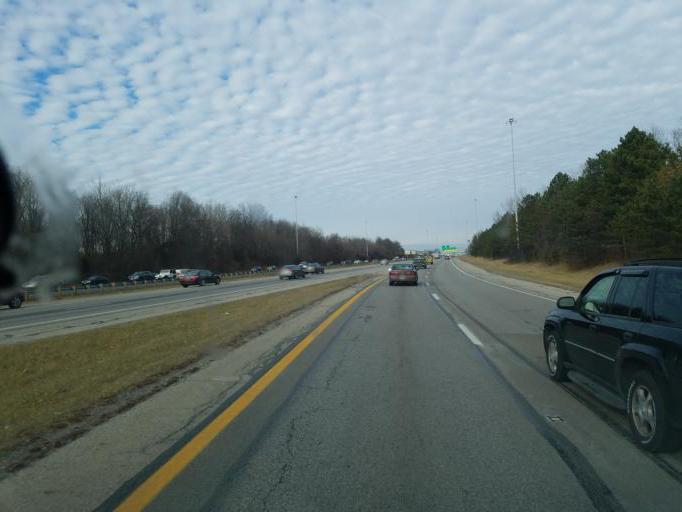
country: US
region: Ohio
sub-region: Franklin County
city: Gahanna
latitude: 40.0209
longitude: -82.9038
